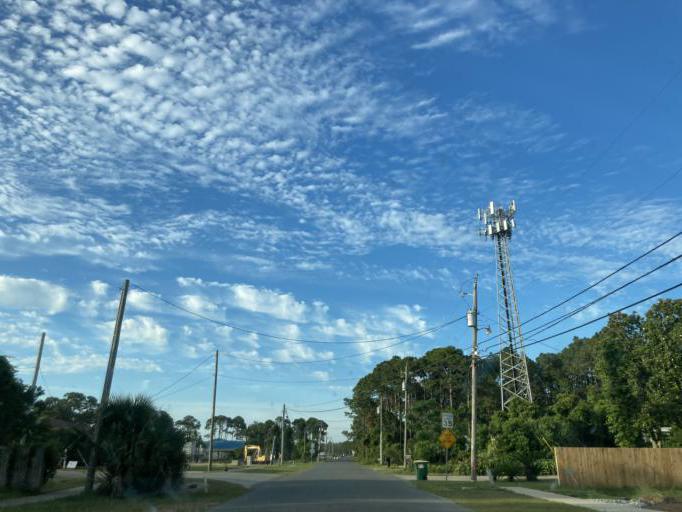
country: US
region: Florida
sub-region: Bay County
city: Panama City Beach
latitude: 30.1940
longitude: -85.8316
